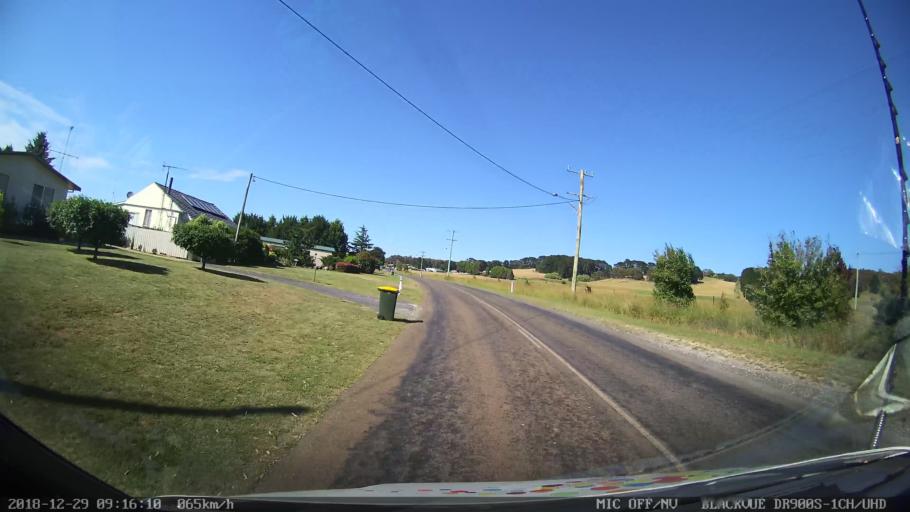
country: AU
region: New South Wales
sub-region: Upper Lachlan Shire
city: Crookwell
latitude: -34.4566
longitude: 149.4535
